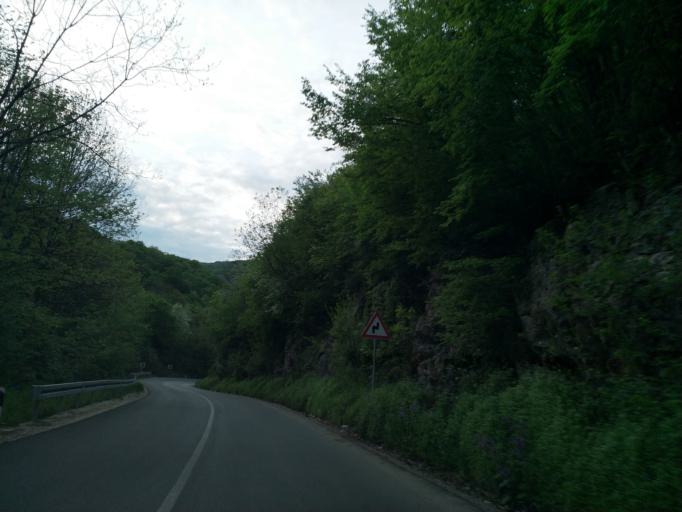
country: RS
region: Central Serbia
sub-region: Pomoravski Okrug
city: Despotovac
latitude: 43.9702
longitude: 21.5252
